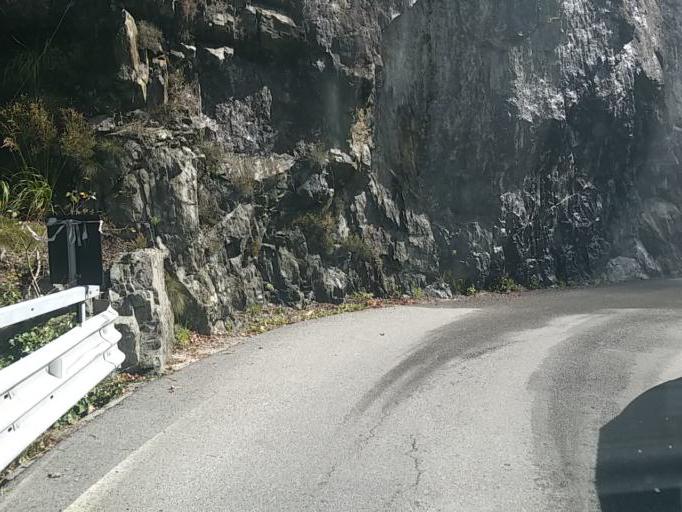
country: IT
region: Piedmont
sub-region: Provincia Verbano-Cusio-Ossola
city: Falmenta
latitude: 46.0752
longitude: 8.6023
